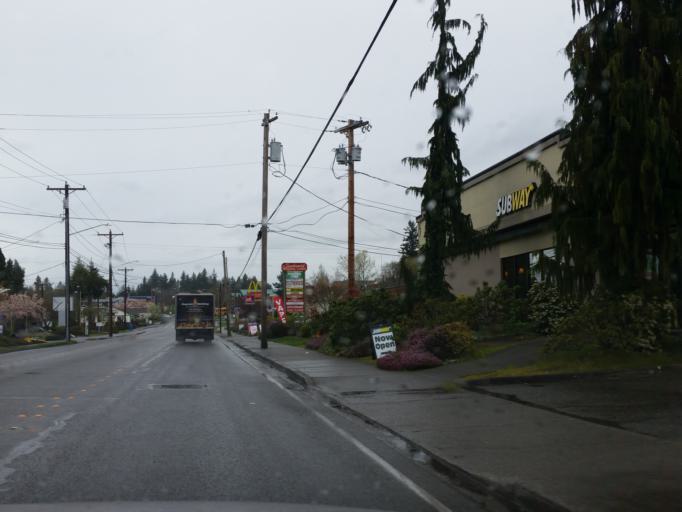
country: US
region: Washington
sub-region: Snohomish County
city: Snohomish
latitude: 47.9215
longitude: -122.0980
